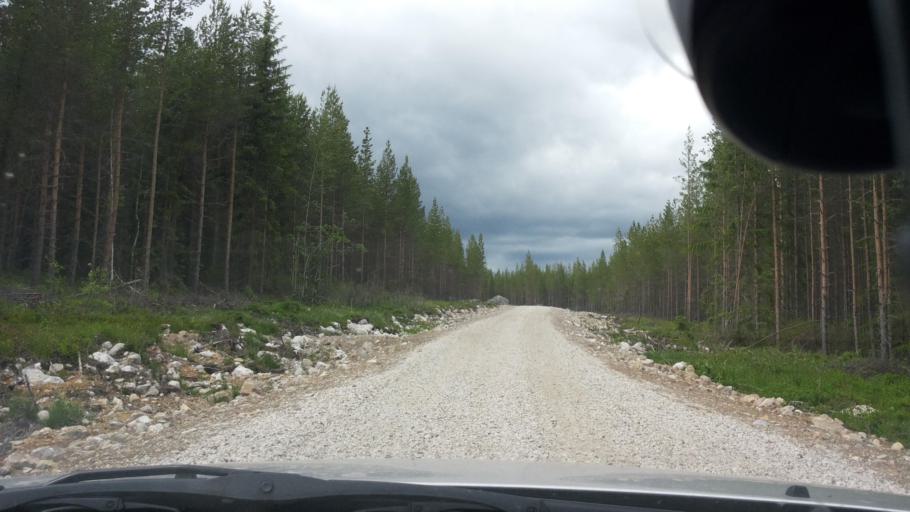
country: SE
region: Gaevleborg
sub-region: Ovanakers Kommun
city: Edsbyn
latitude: 61.4632
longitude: 15.2913
